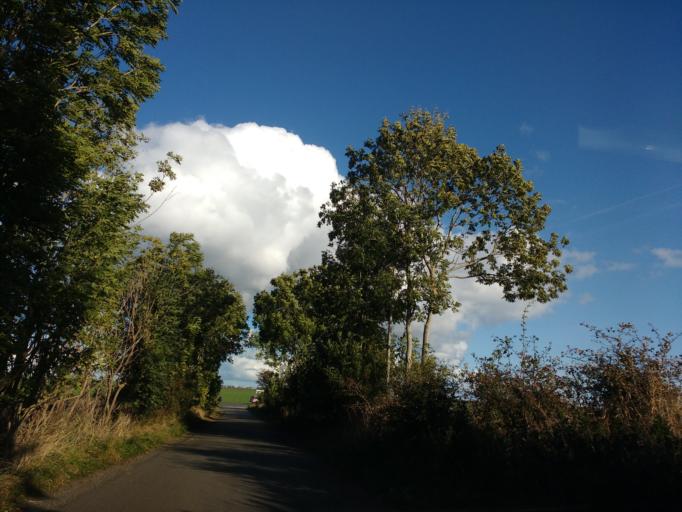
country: DE
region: Schleswig-Holstein
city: Grossenbrode
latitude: 54.4305
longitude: 11.1147
